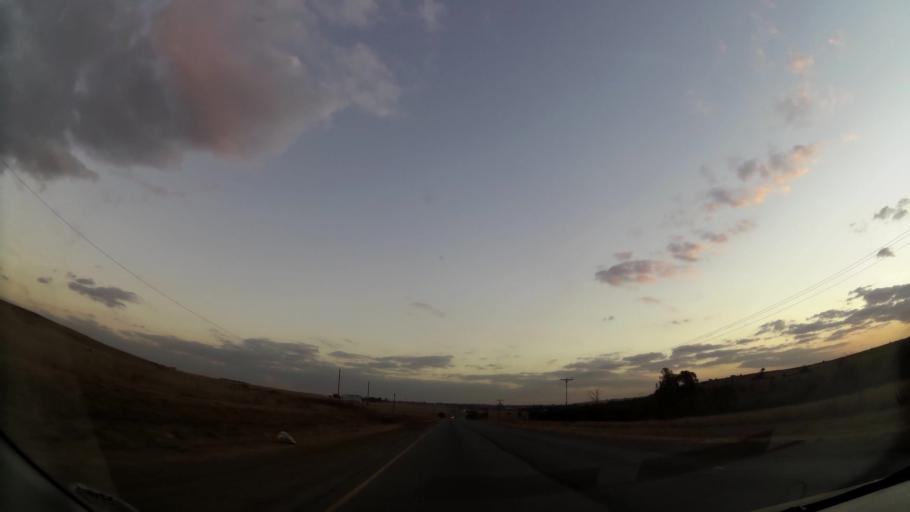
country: ZA
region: Gauteng
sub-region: West Rand District Municipality
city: Krugersdorp
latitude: -26.0488
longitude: 27.7139
